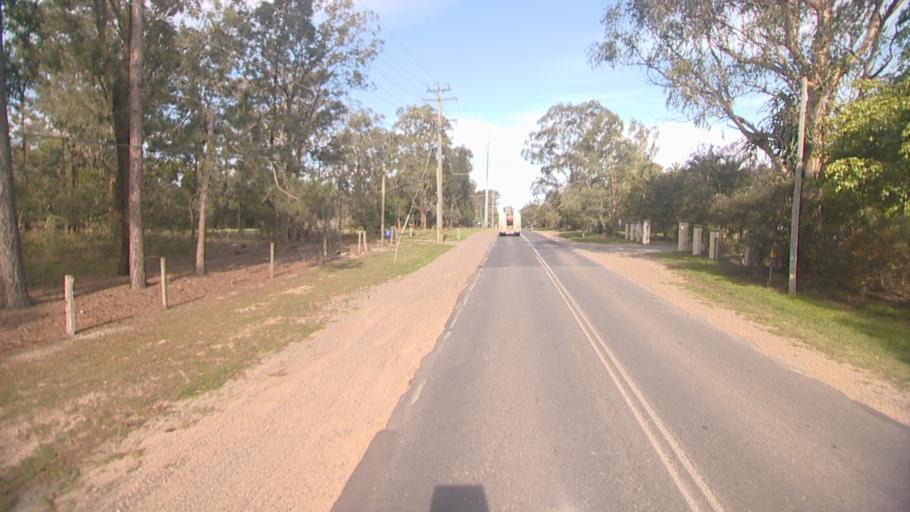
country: AU
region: Queensland
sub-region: Logan
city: Logan Reserve
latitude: -27.7047
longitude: 153.0637
